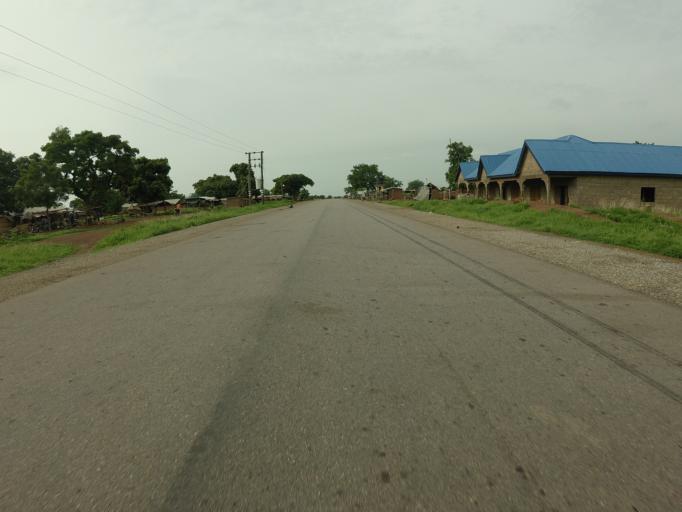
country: GH
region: Northern
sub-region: Yendi
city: Yendi
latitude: 9.8116
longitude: -0.1153
